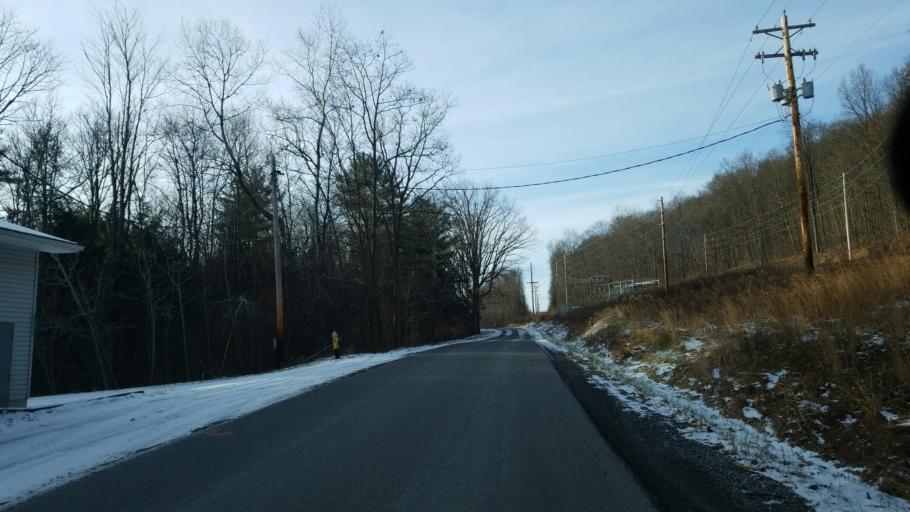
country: US
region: Pennsylvania
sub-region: Clearfield County
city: Treasure Lake
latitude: 41.1021
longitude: -78.6741
